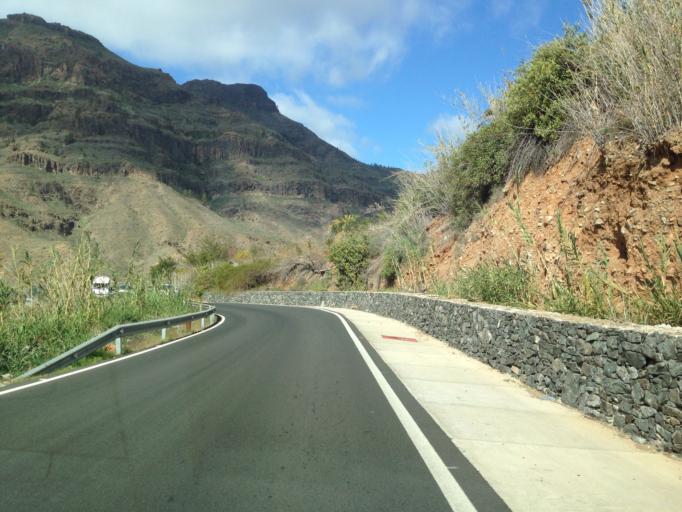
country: ES
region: Canary Islands
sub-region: Provincia de Las Palmas
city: Santa Lucia
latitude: 27.8741
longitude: -15.5655
